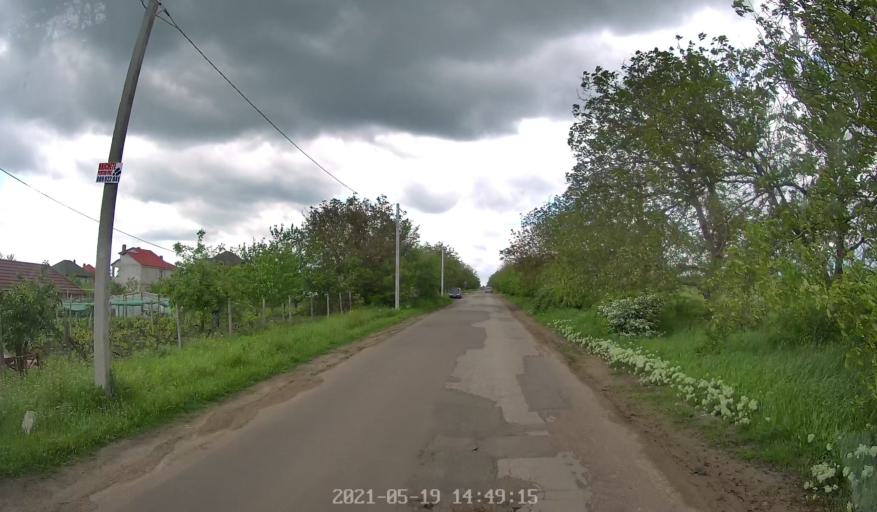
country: MD
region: Chisinau
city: Stauceni
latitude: 47.0484
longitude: 28.9531
